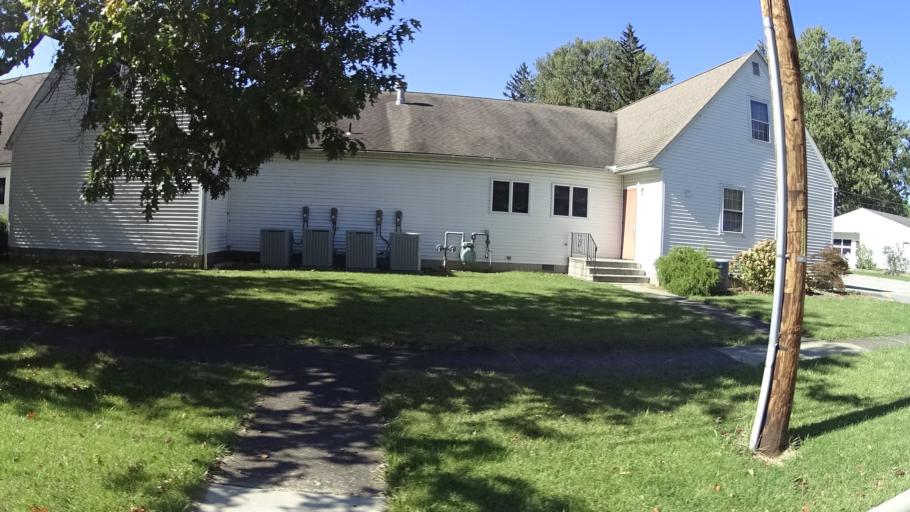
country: US
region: Ohio
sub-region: Lorain County
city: Oberlin
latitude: 41.2948
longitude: -82.2282
